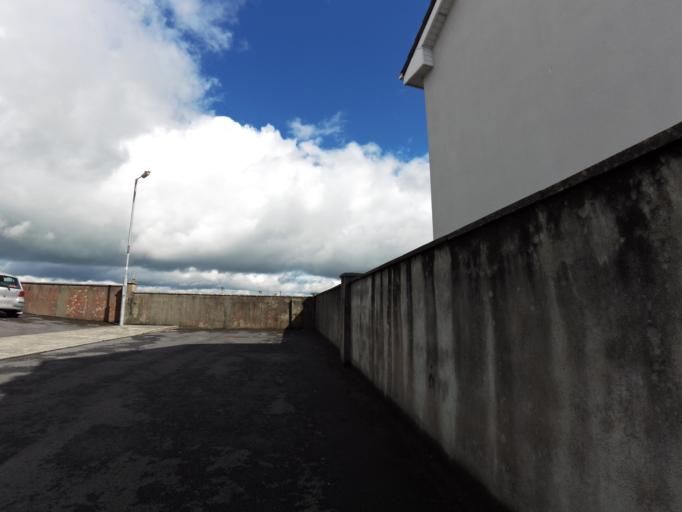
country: IE
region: Connaught
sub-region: County Galway
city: Loughrea
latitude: 53.2052
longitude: -8.5769
